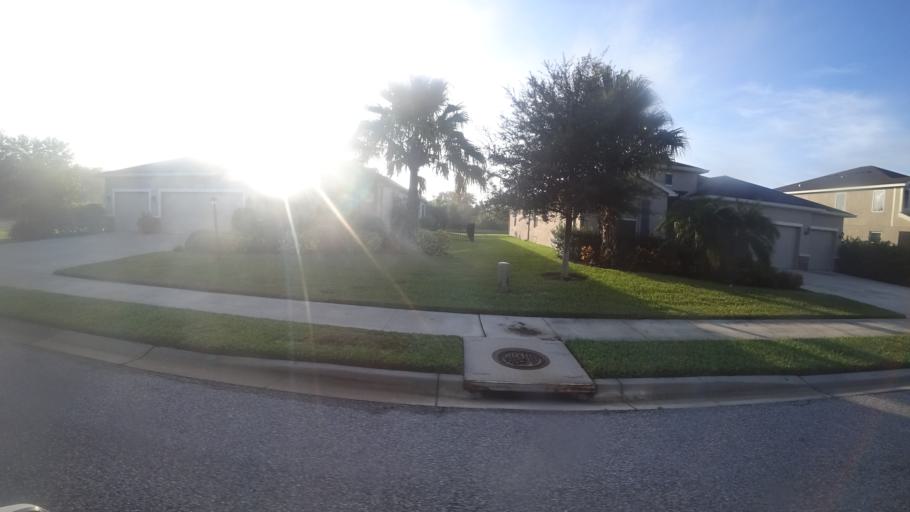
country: US
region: Florida
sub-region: Manatee County
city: Ellenton
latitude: 27.5400
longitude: -82.4118
